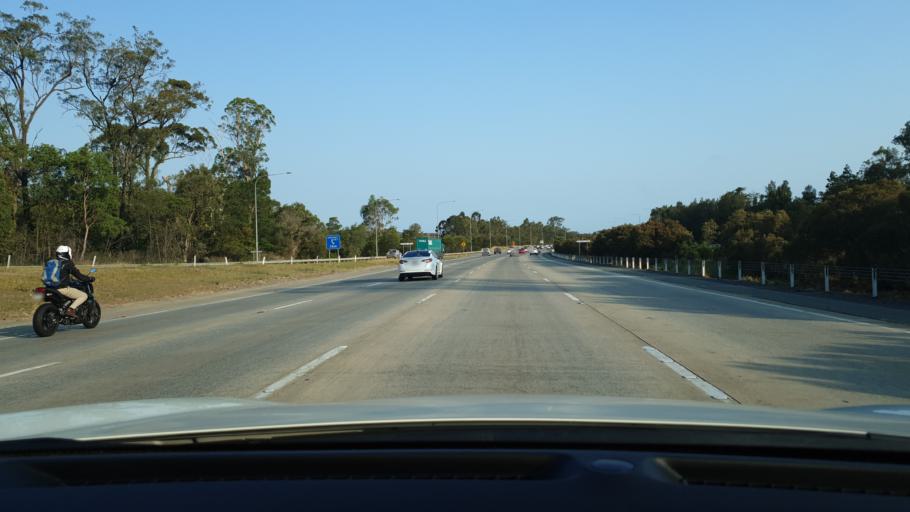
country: AU
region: Queensland
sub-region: Gold Coast
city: Ormeau Hills
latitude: -27.7587
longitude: 153.2430
